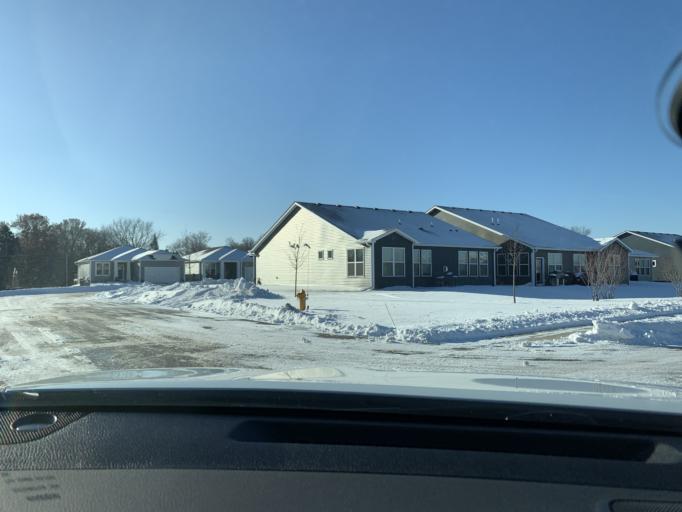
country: US
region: Minnesota
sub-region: Anoka County
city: Fridley
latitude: 45.0944
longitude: -93.2592
